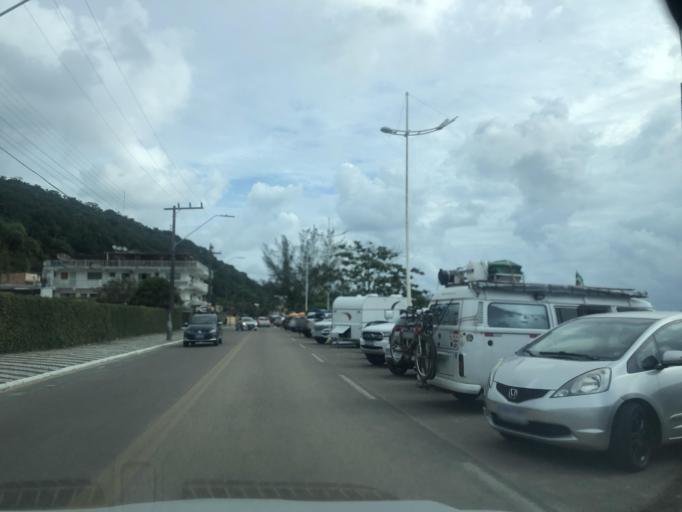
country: BR
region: Santa Catarina
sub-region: Sao Francisco Do Sul
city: Sao Francisco do Sul
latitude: -26.2206
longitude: -48.5013
